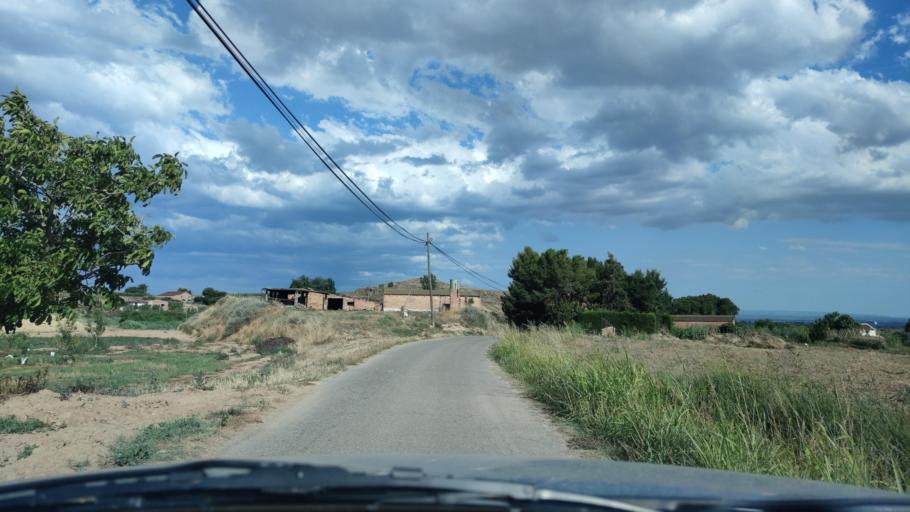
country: ES
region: Catalonia
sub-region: Provincia de Lleida
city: Alpicat
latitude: 41.6320
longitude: 0.5563
